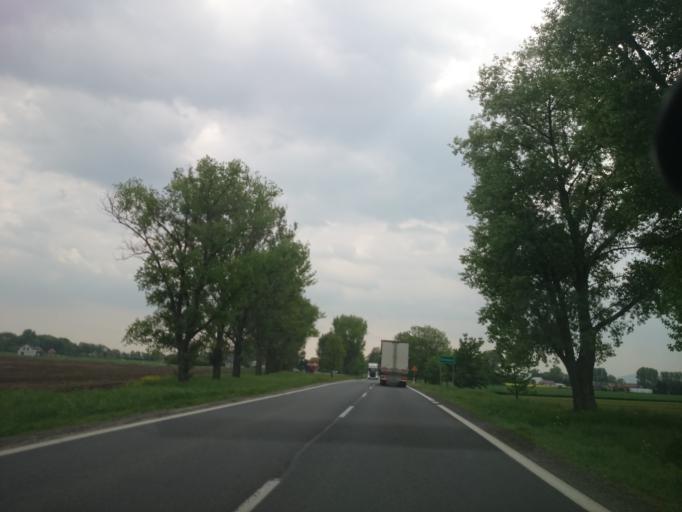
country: PL
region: Lower Silesian Voivodeship
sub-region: Powiat wroclawski
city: Kobierzyce
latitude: 50.9448
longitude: 16.9036
